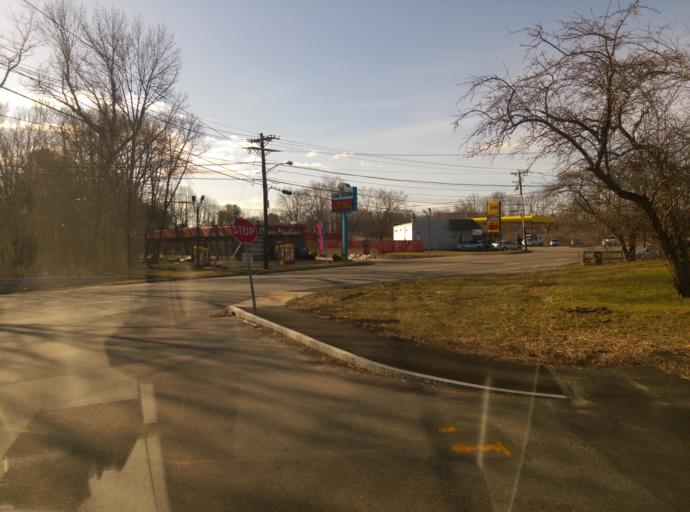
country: US
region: Massachusetts
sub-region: Essex County
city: Haverhill
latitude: 42.7443
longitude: -71.1102
